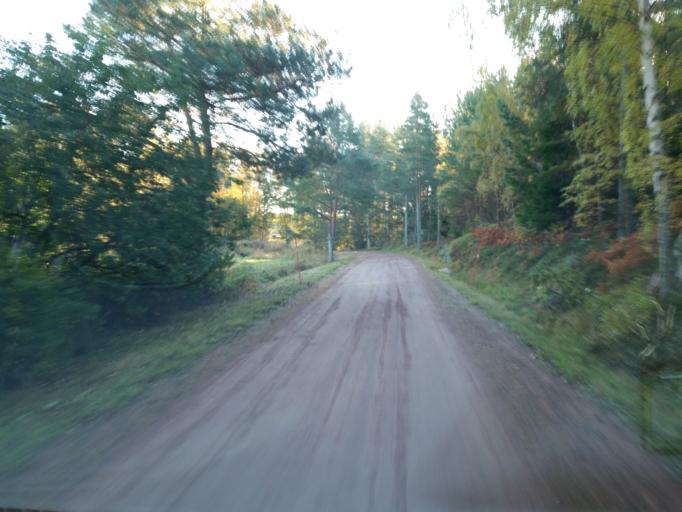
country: AX
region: Alands skaergard
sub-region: Vardoe
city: Vardoe
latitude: 60.2424
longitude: 20.3318
